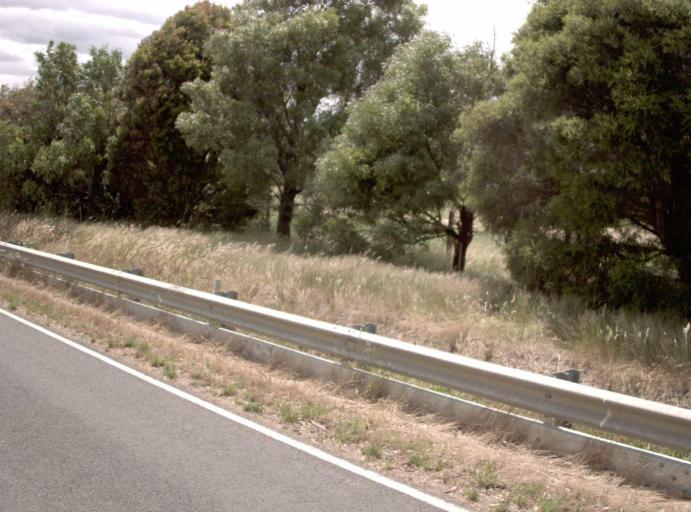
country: AU
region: Victoria
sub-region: Latrobe
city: Moe
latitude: -38.1089
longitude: 146.1571
